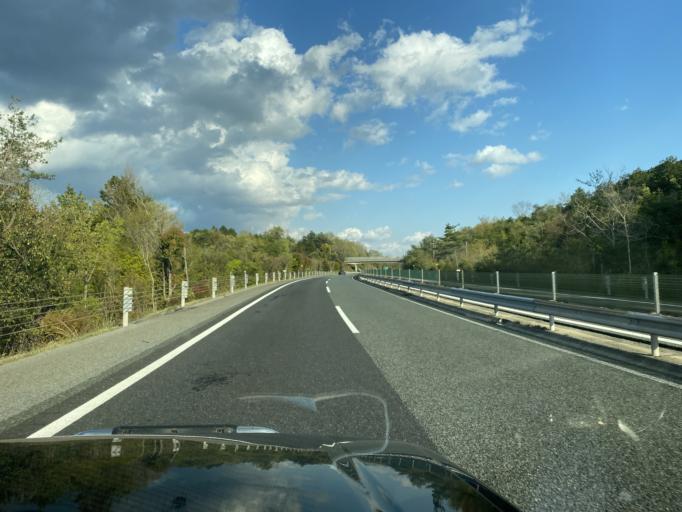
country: JP
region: Hyogo
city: Sandacho
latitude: 34.9424
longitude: 135.1531
